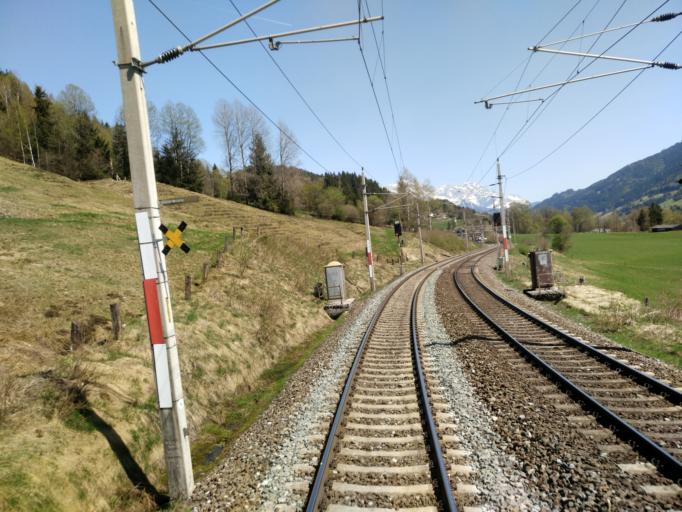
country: AT
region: Salzburg
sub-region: Politischer Bezirk Zell am See
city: Leogang
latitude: 47.4438
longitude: 12.7307
